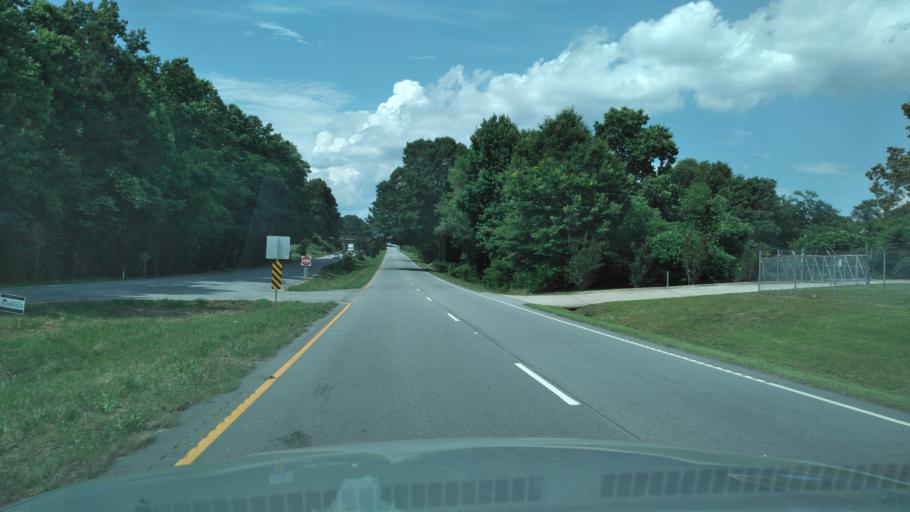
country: US
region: South Carolina
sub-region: Spartanburg County
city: Roebuck
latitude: 34.8640
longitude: -81.9613
